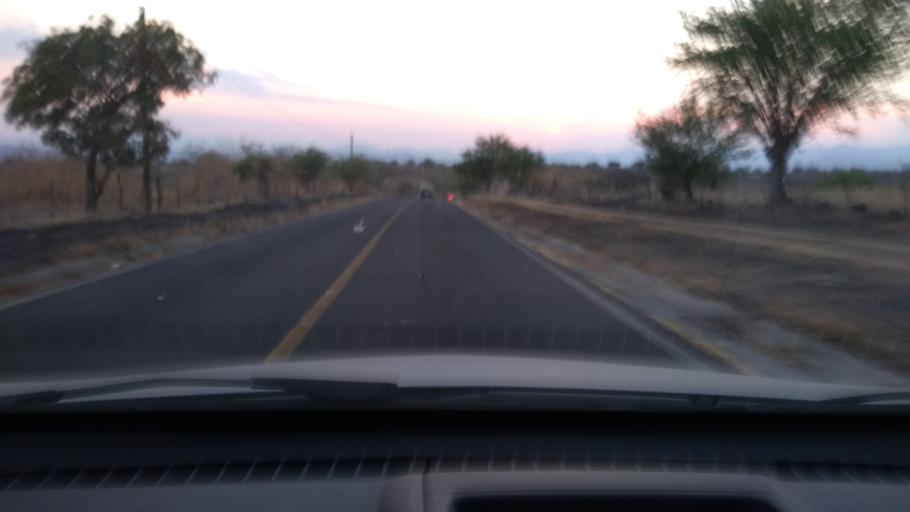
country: MX
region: Morelos
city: Coatetelco
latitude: 18.7231
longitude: -99.2928
